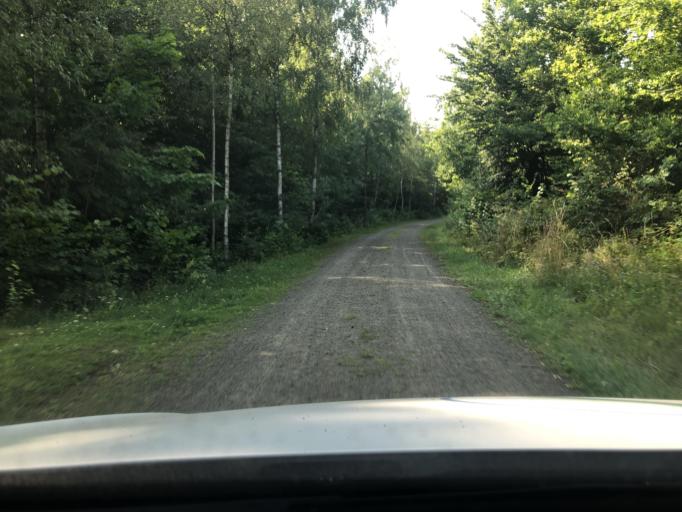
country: SE
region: Skane
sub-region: Kristianstads Kommun
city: Degeberga
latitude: 55.8026
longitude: 14.1405
